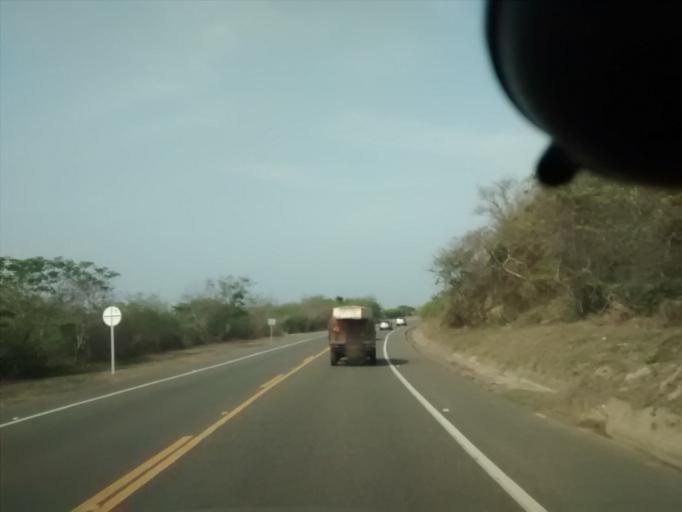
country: CO
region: Bolivar
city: Clemencia
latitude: 10.6560
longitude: -75.3898
